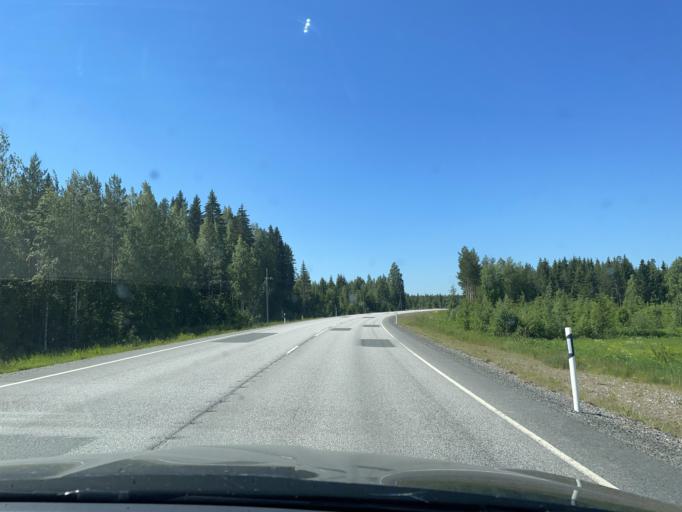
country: FI
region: Central Finland
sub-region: Saarijaervi-Viitasaari
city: Viitasaari
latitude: 63.1681
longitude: 25.9945
